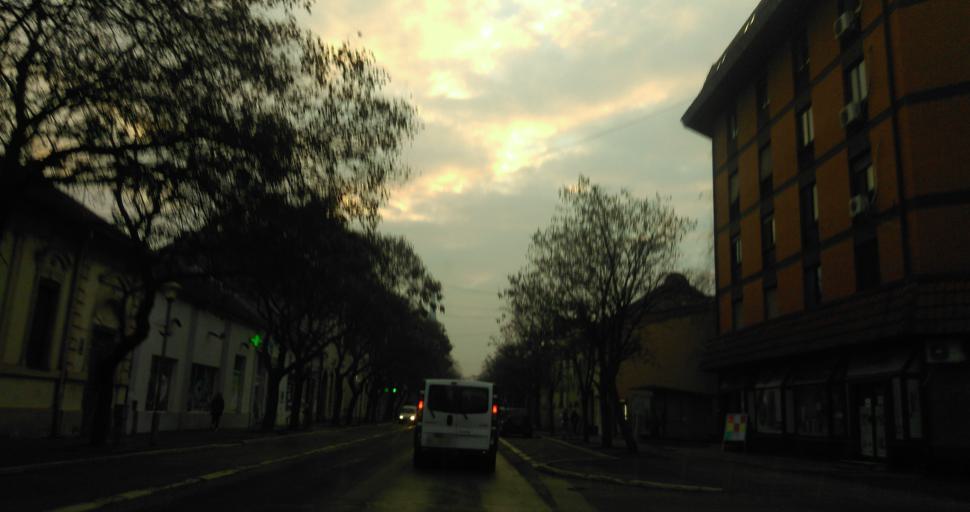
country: RS
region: Autonomna Pokrajina Vojvodina
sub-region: Juznobacki Okrug
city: Becej
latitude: 45.6174
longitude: 20.0457
